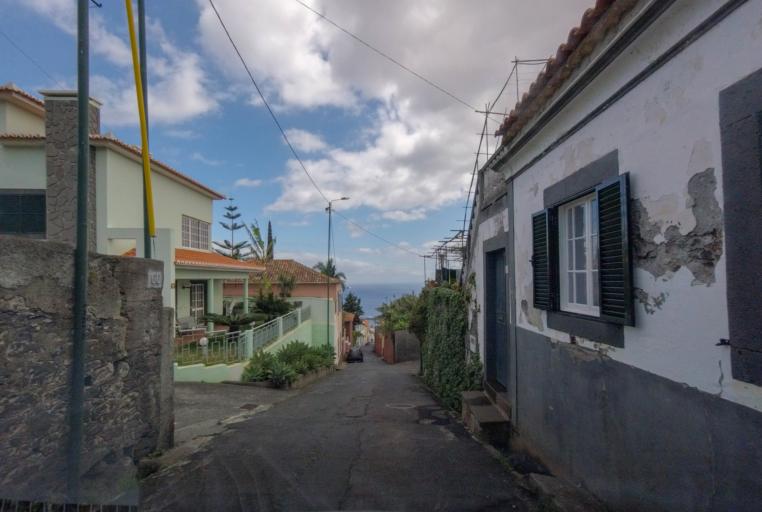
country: PT
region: Madeira
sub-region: Funchal
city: Nossa Senhora do Monte
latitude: 32.6629
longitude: -16.9049
